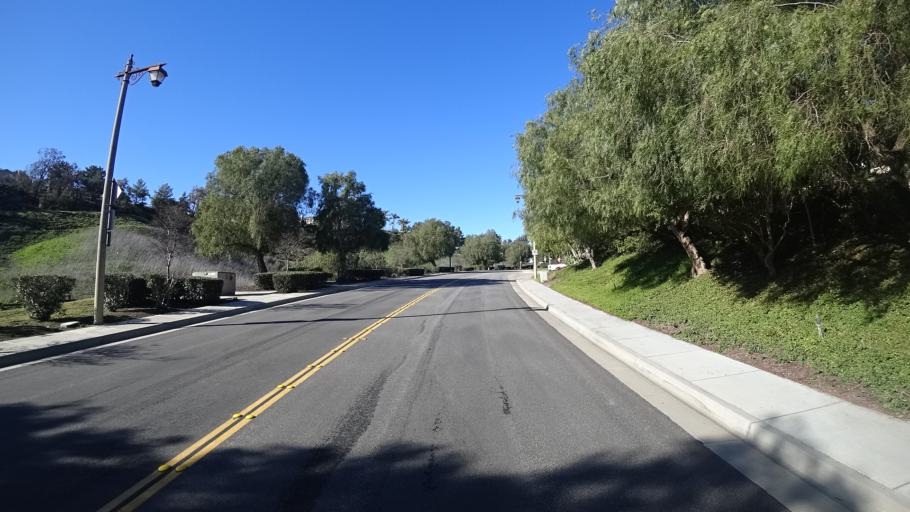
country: US
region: California
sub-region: Orange County
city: Yorba Linda
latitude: 33.8579
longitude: -117.7435
